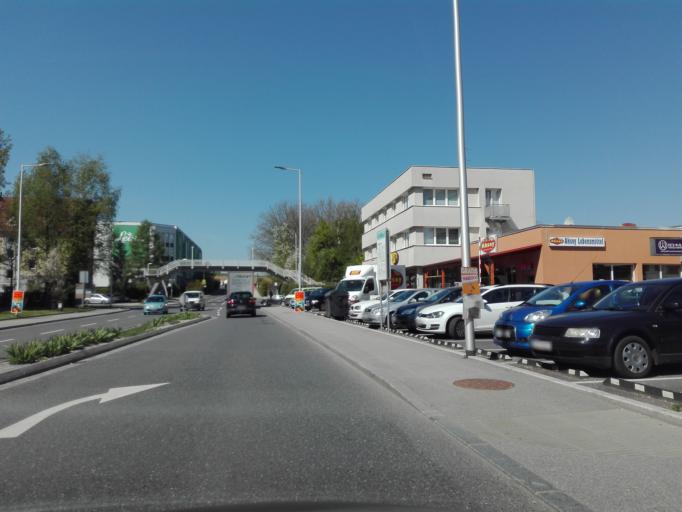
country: AT
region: Upper Austria
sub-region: Steyr Stadt
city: Steyr
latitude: 48.0504
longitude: 14.4178
